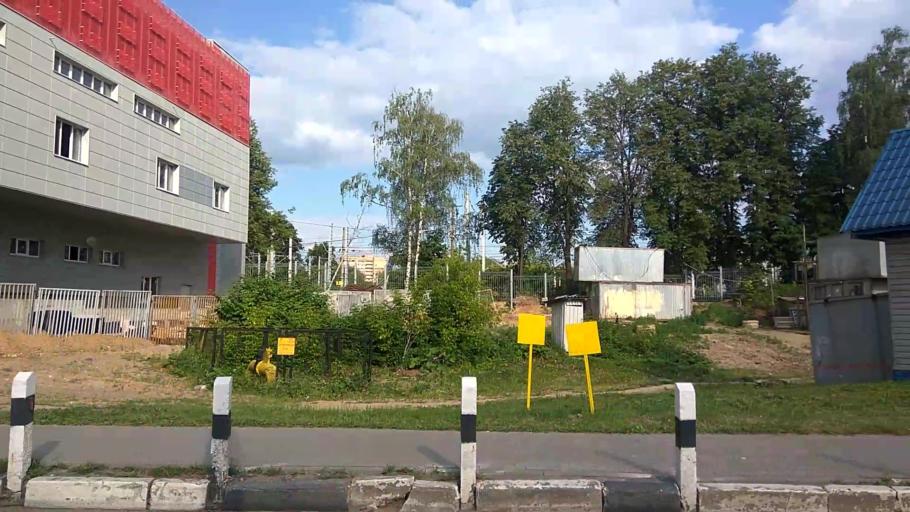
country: RU
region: Moskovskaya
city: Mytishchi
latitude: 55.9247
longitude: 37.7718
